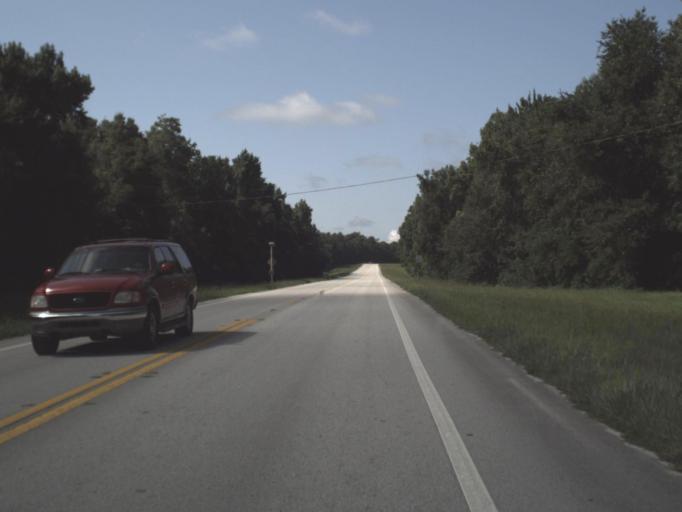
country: US
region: Florida
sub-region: Hernando County
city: North Brooksville
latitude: 28.5905
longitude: -82.4160
